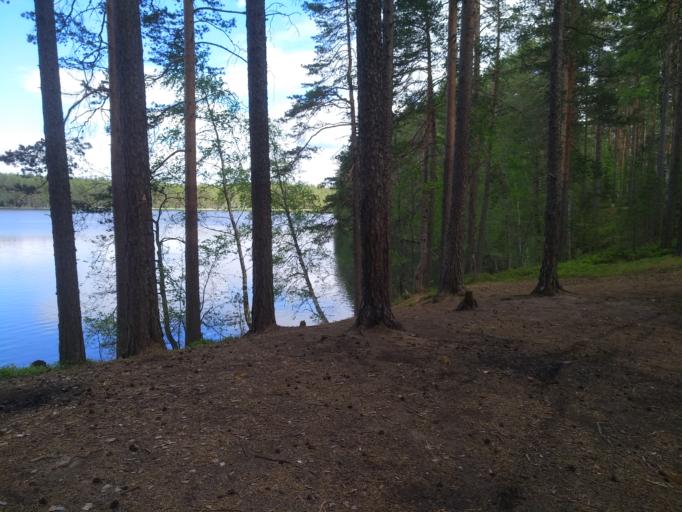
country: RU
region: Leningrad
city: Michurinskoye
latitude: 60.5939
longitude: 29.8878
